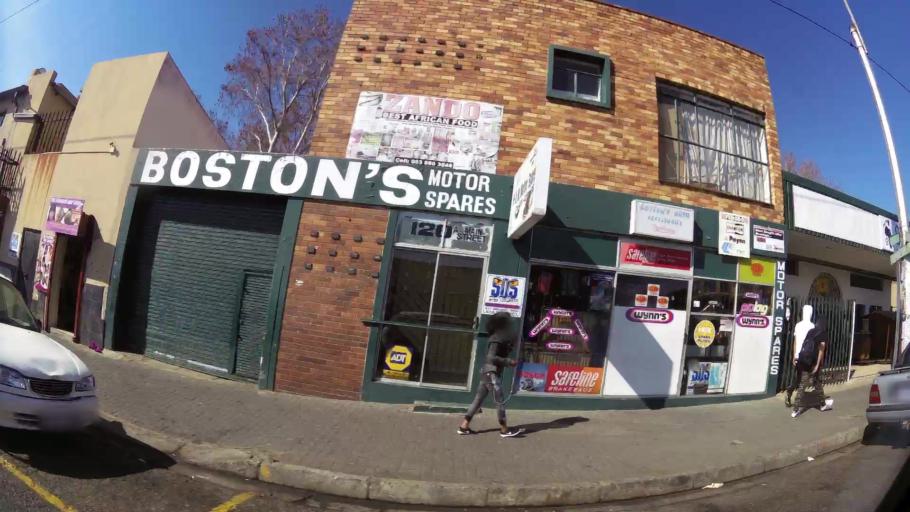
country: ZA
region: Gauteng
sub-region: City of Johannesburg Metropolitan Municipality
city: Johannesburg
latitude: -26.2507
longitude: 28.0517
